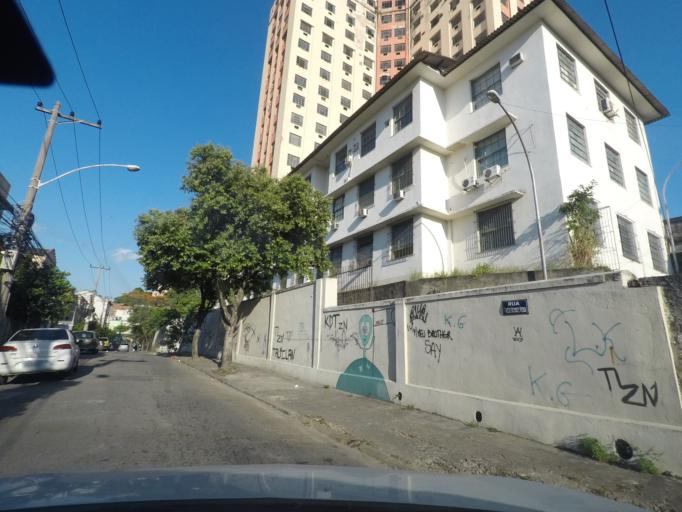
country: BR
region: Rio de Janeiro
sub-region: Rio De Janeiro
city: Rio de Janeiro
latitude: -22.9023
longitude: -43.2236
